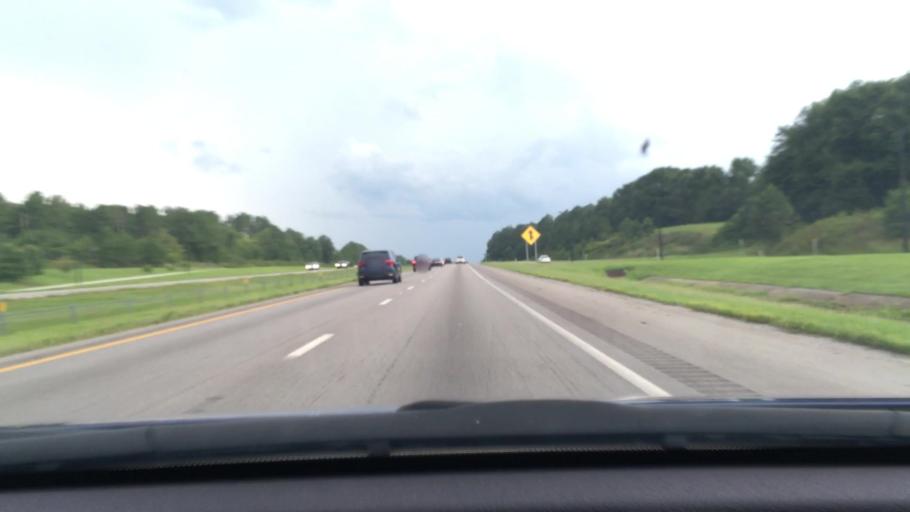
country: US
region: South Carolina
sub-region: Kershaw County
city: Lugoff
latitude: 34.1999
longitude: -80.6637
